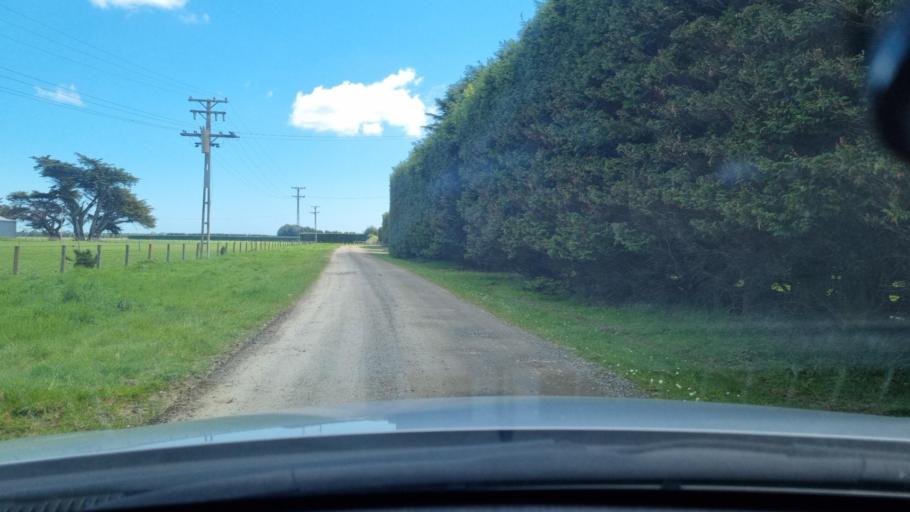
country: NZ
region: Southland
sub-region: Invercargill City
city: Invercargill
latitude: -46.3602
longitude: 168.3031
